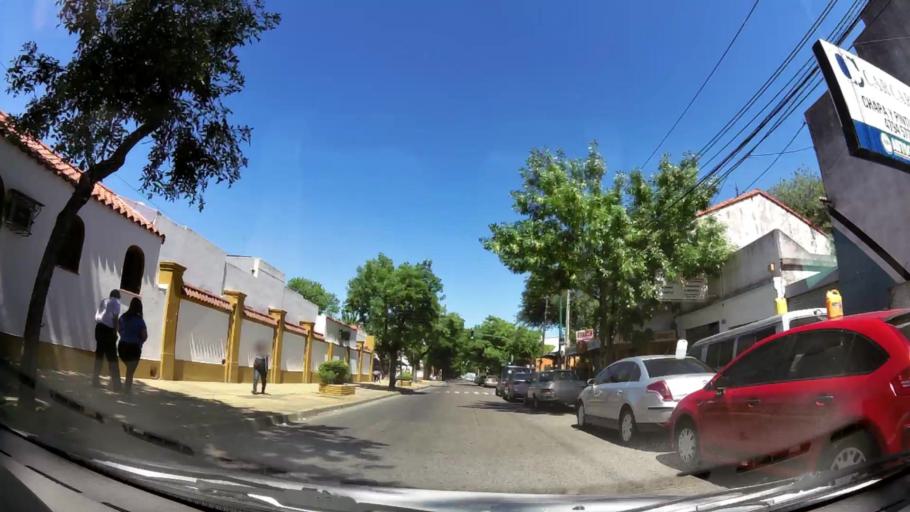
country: AR
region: Buenos Aires
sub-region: Partido de Vicente Lopez
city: Olivos
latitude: -34.5154
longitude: -58.5079
